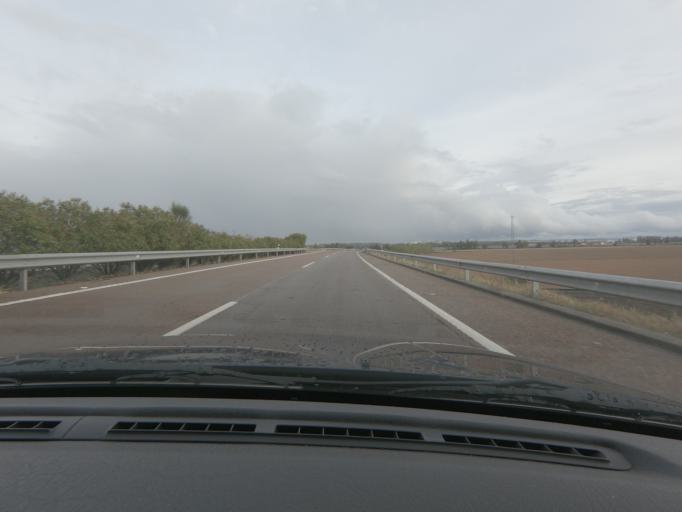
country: ES
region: Extremadura
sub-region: Provincia de Badajoz
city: Badajoz
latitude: 38.9167
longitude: -6.9526
